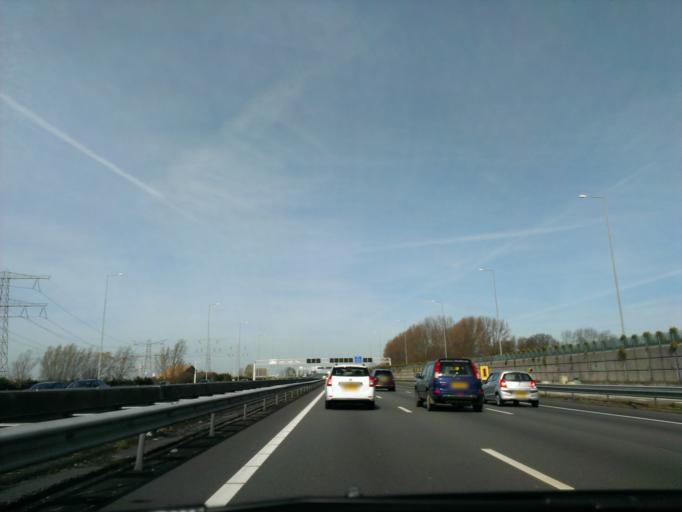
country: NL
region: North Holland
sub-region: Gemeente Weesp
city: Weesp
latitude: 52.3234
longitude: 5.0763
